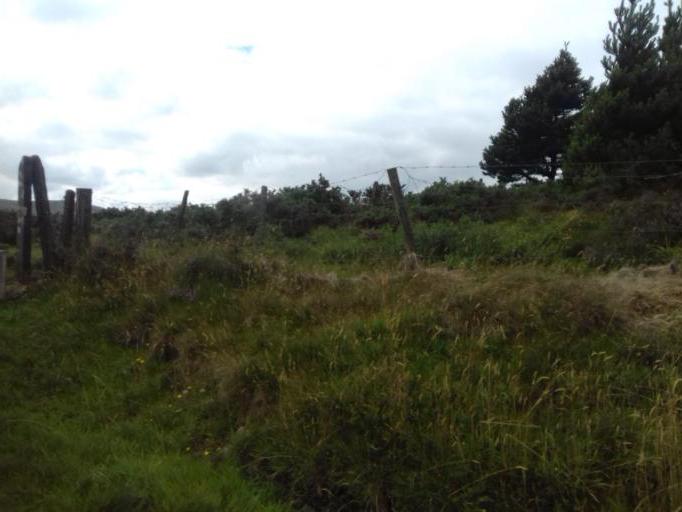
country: IE
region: Leinster
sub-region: Loch Garman
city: Bunclody
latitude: 52.6516
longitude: -6.7701
